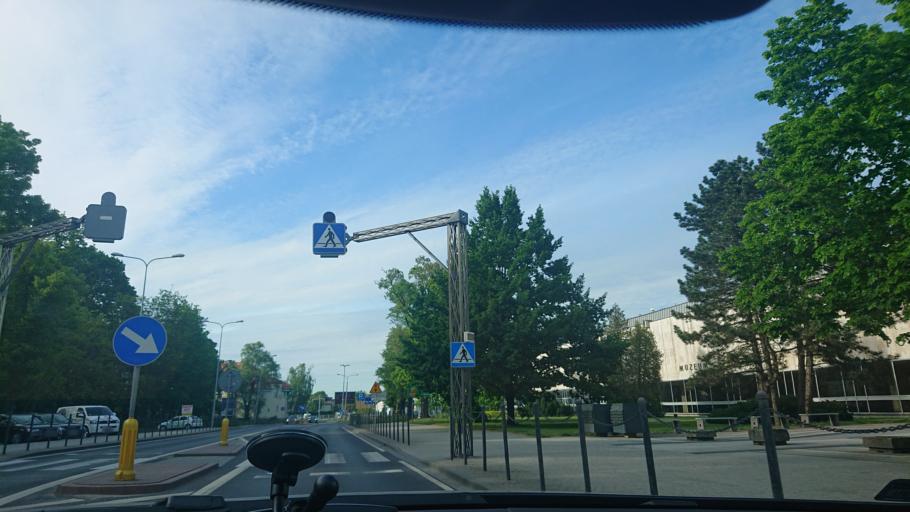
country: PL
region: Greater Poland Voivodeship
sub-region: Powiat gnieznienski
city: Gniezno
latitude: 52.5332
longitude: 17.5827
